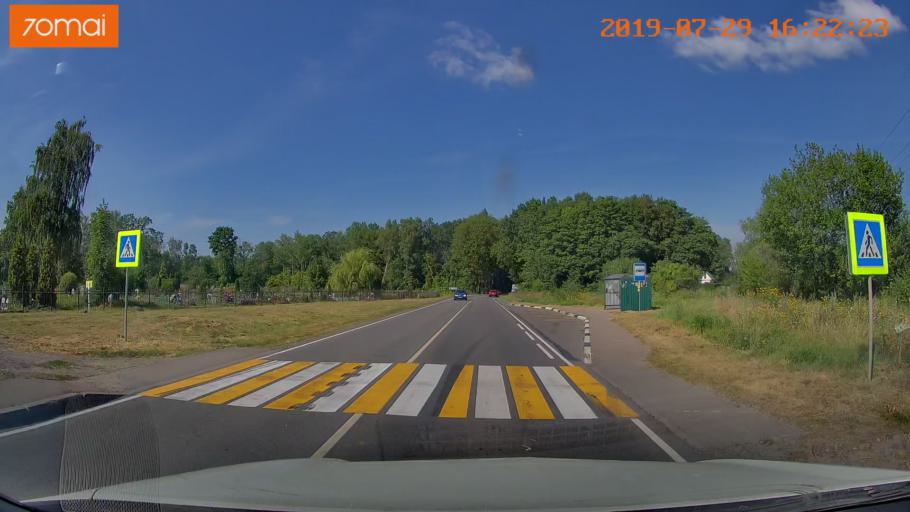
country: RU
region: Kaliningrad
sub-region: Gorod Kaliningrad
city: Baltiysk
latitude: 54.6975
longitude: 19.9386
